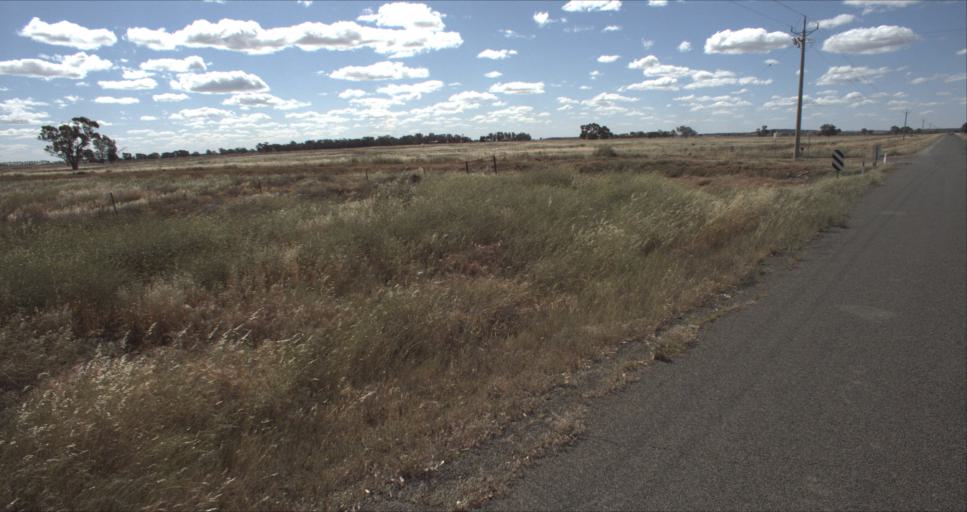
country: AU
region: New South Wales
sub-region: Leeton
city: Leeton
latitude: -34.4717
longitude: 146.2508
